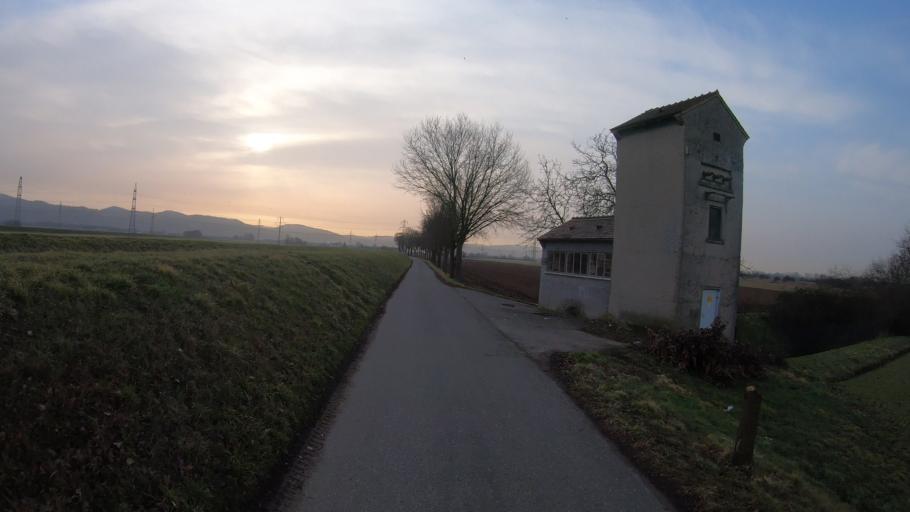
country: DE
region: Baden-Wuerttemberg
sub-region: Karlsruhe Region
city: Hemsbach
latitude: 49.5864
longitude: 8.6072
